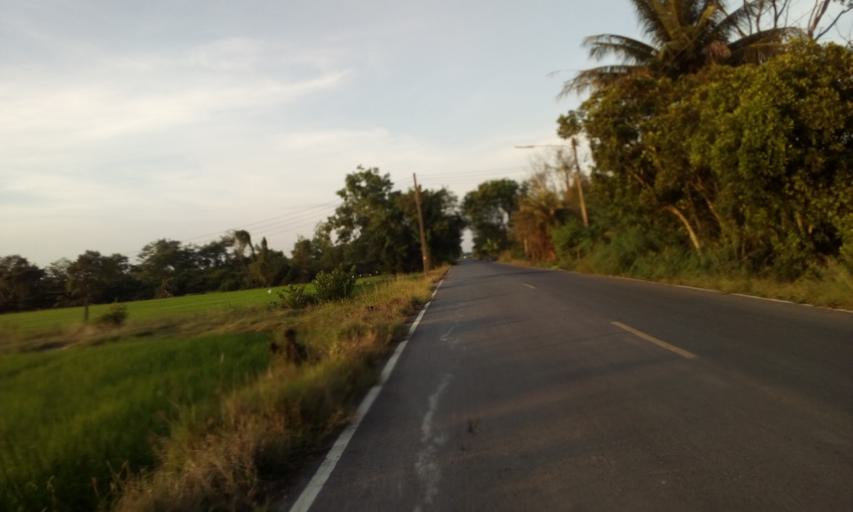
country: TH
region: Pathum Thani
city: Nong Suea
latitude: 14.0483
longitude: 100.8670
